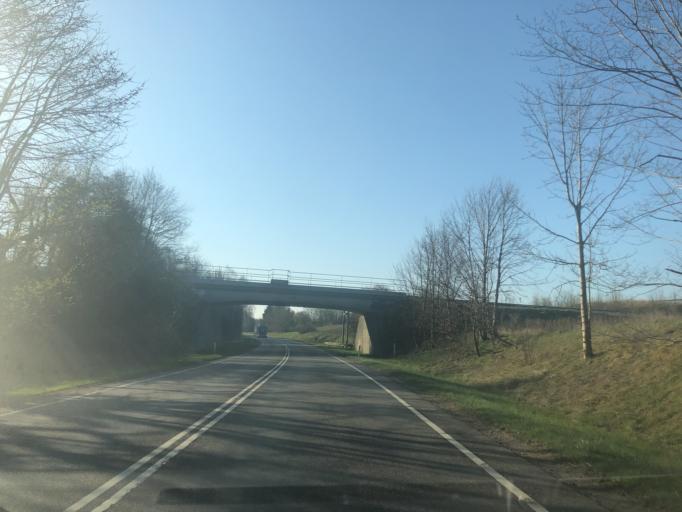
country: DK
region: Zealand
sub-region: Faxe Kommune
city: Haslev
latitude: 55.3232
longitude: 11.9424
